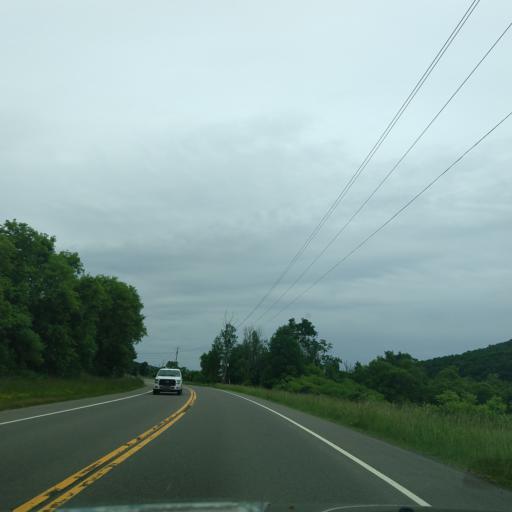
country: US
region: New York
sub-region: Cortland County
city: McGraw
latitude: 42.4839
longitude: -76.0671
